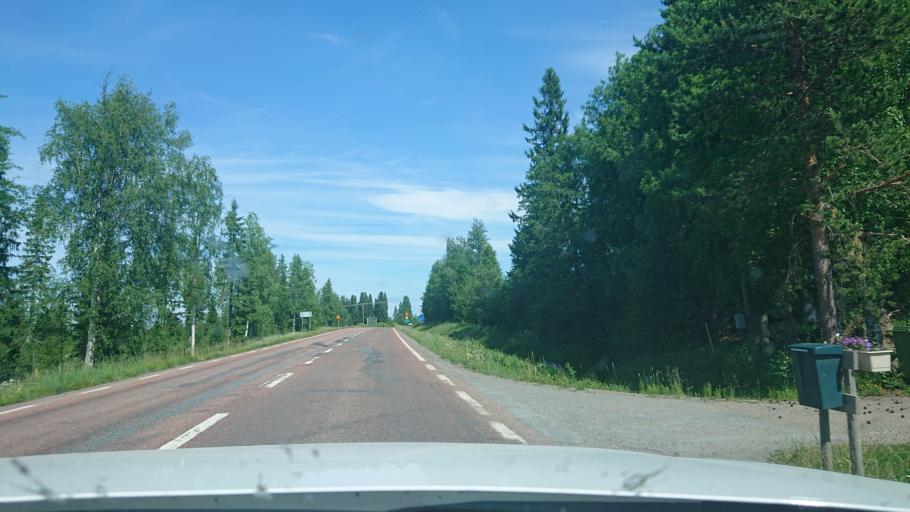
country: SE
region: Jaemtland
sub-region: Stroemsunds Kommun
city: Stroemsund
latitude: 63.8631
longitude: 15.5697
